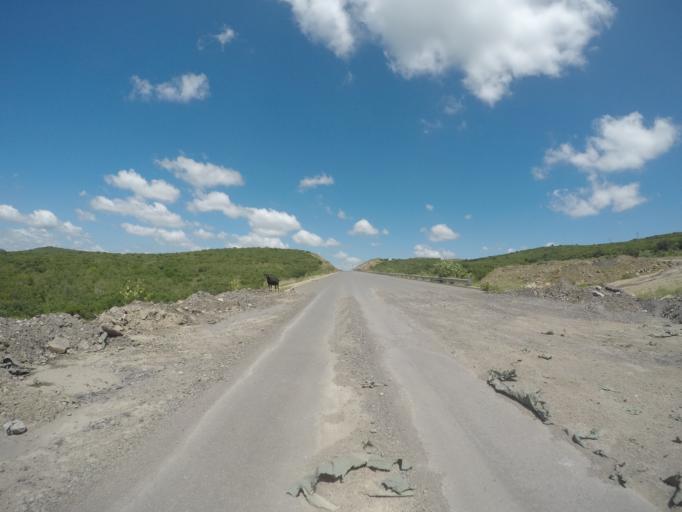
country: ZA
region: KwaZulu-Natal
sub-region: uThungulu District Municipality
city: Empangeni
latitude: -28.6238
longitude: 31.7576
